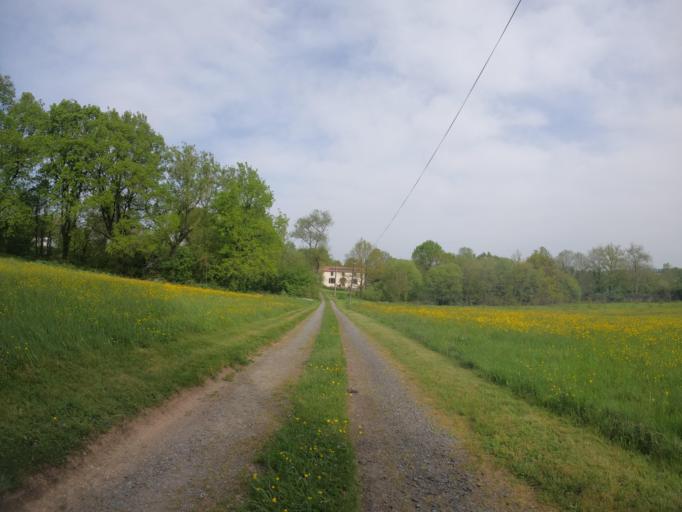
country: FR
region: Poitou-Charentes
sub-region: Departement des Deux-Sevres
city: La Chapelle-Saint-Laurent
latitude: 46.6952
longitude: -0.5088
